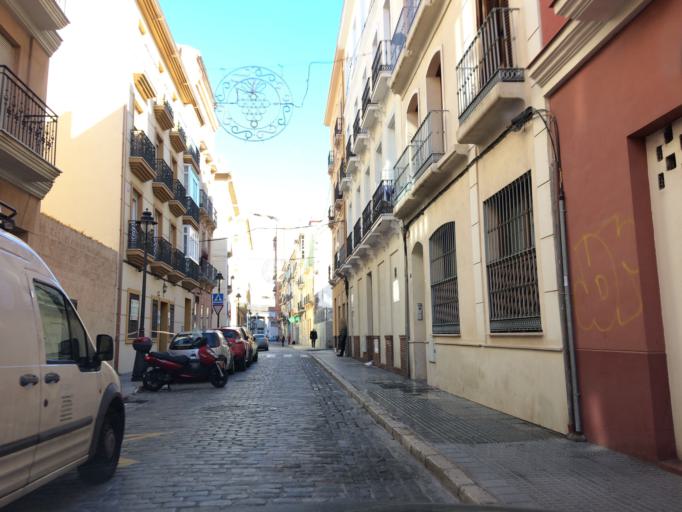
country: ES
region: Andalusia
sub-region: Provincia de Malaga
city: Malaga
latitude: 36.7144
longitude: -4.4287
